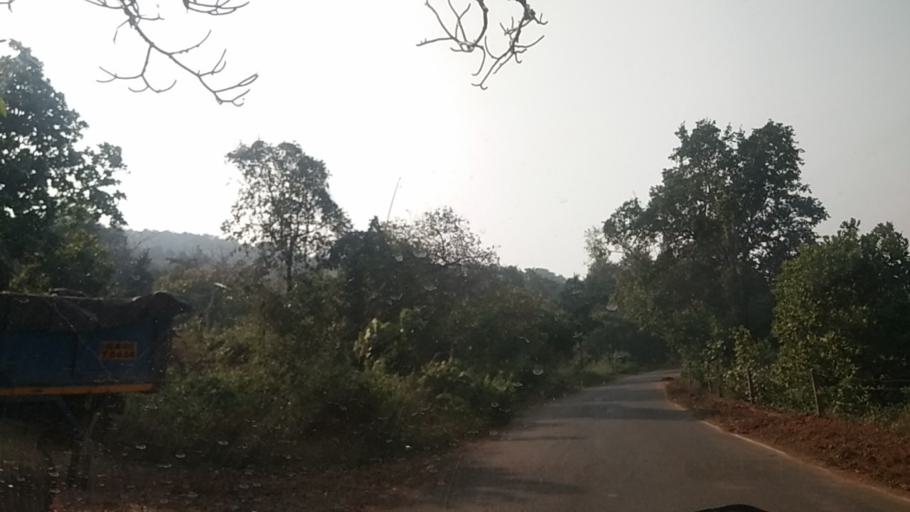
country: IN
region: Goa
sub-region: North Goa
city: Pernem
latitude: 15.7301
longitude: 73.7684
